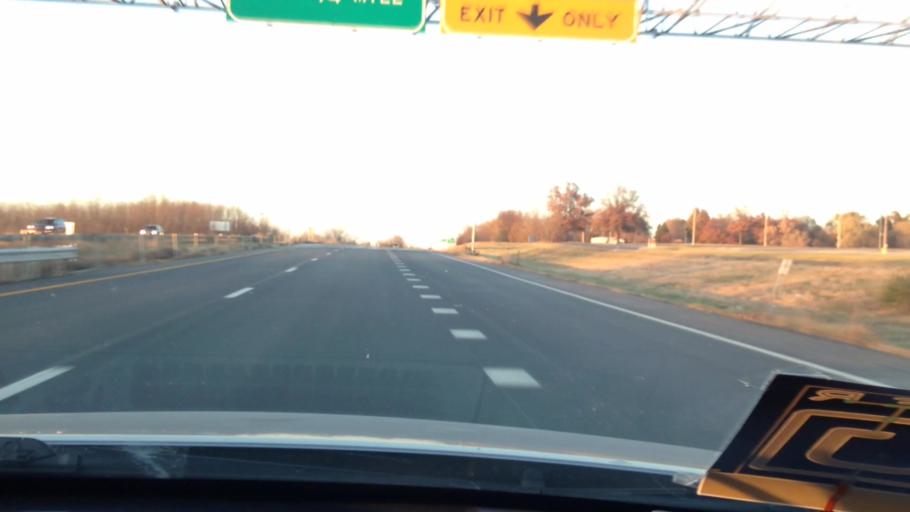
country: US
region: Missouri
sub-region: Clay County
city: Gladstone
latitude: 39.2498
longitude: -94.5902
